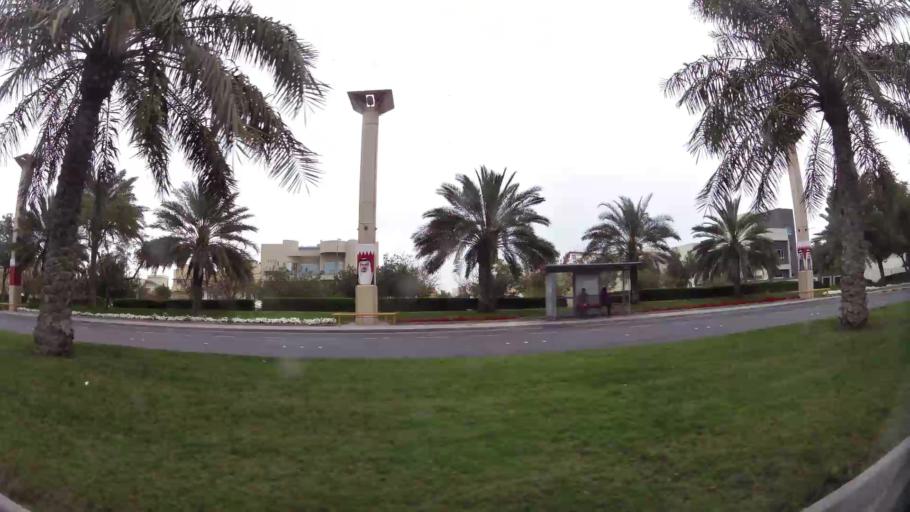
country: BH
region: Northern
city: Ar Rifa'
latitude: 26.1294
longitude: 50.5373
